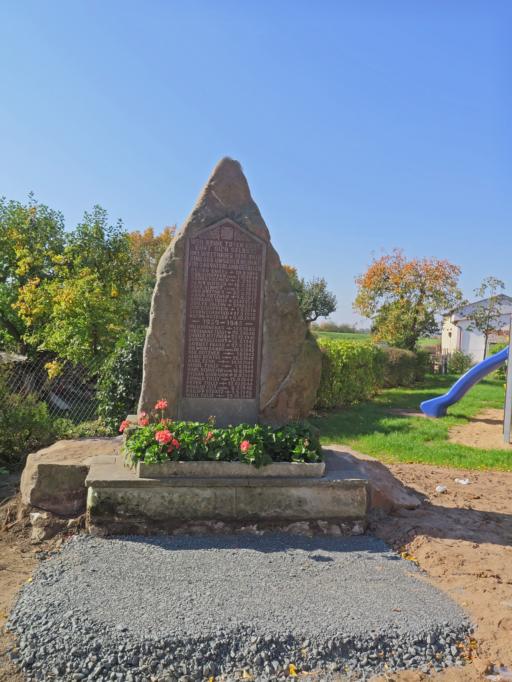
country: DE
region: Bavaria
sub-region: Regierungsbezirk Unterfranken
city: Ebelsbach
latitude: 49.9942
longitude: 10.6405
